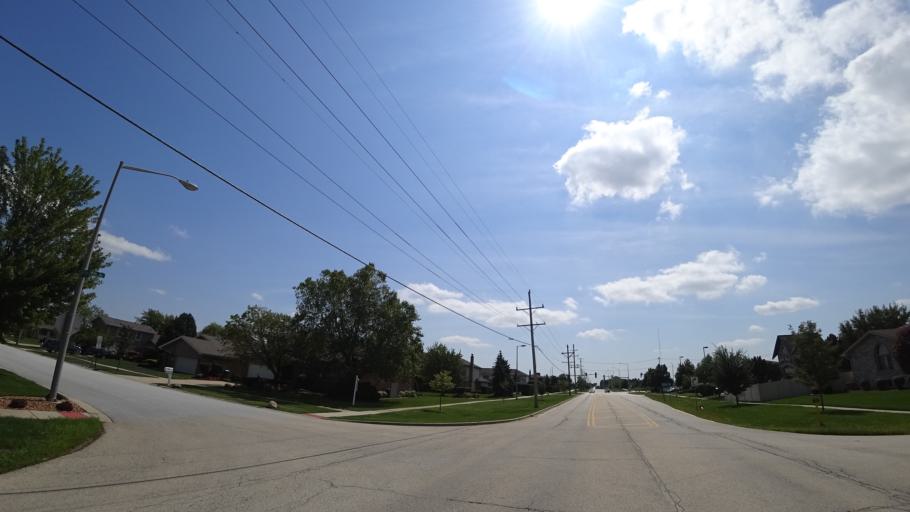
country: US
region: Illinois
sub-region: Cook County
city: Orland Hills
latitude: 41.5665
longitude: -87.8467
